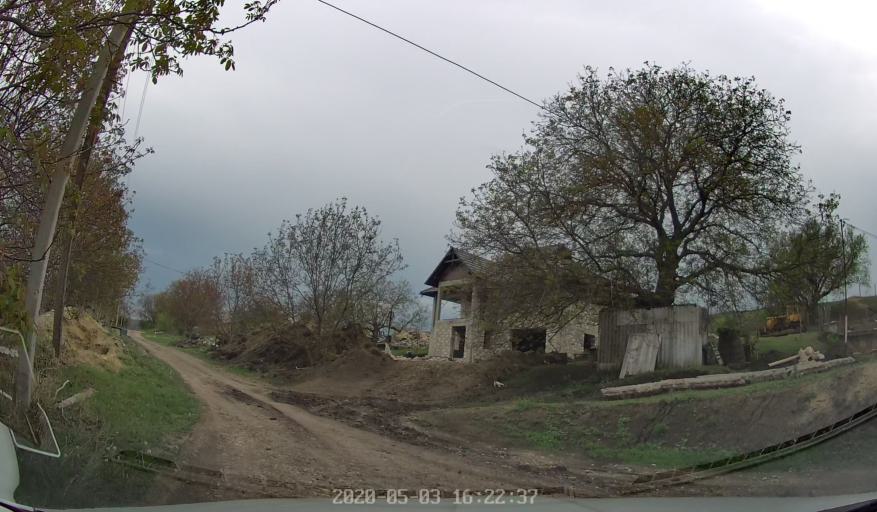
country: MD
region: Calarasi
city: Calarasi
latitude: 47.1991
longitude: 28.3473
